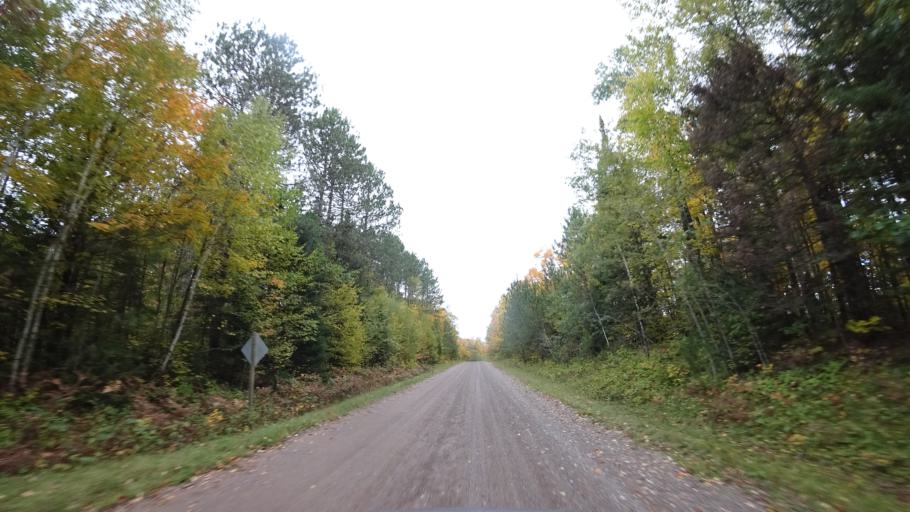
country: US
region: Wisconsin
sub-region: Sawyer County
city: Little Round Lake
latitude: 45.9641
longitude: -90.9808
